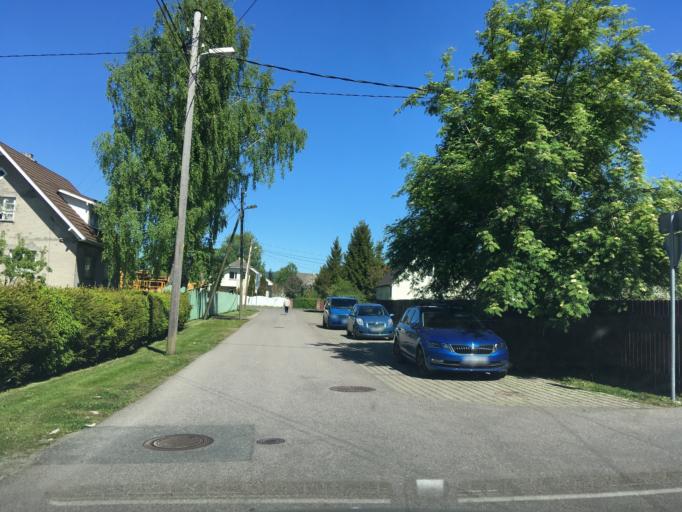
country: EE
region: Harju
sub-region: Tallinna linn
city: Tallinn
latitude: 59.4123
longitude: 24.7483
